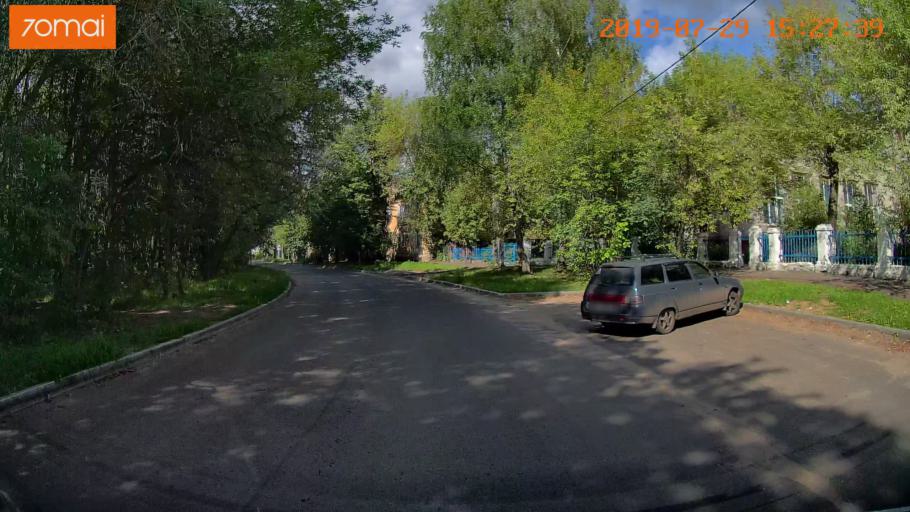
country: RU
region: Ivanovo
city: Bogorodskoye
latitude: 57.0240
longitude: 41.0102
